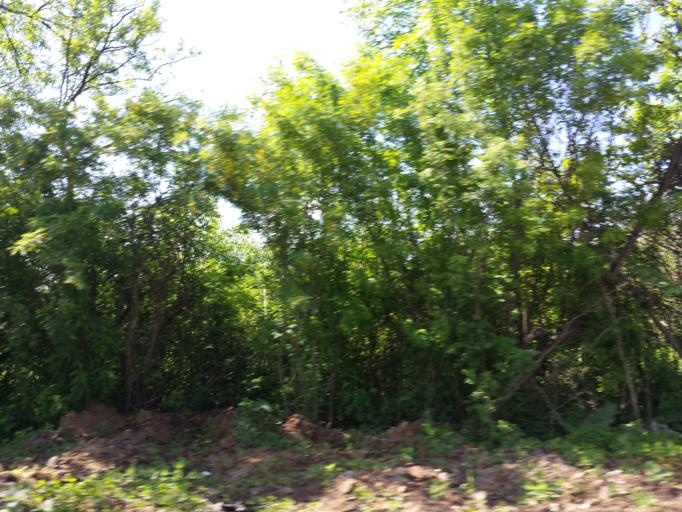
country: RU
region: Moskovskaya
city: Povedniki
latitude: 55.9312
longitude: 37.6150
